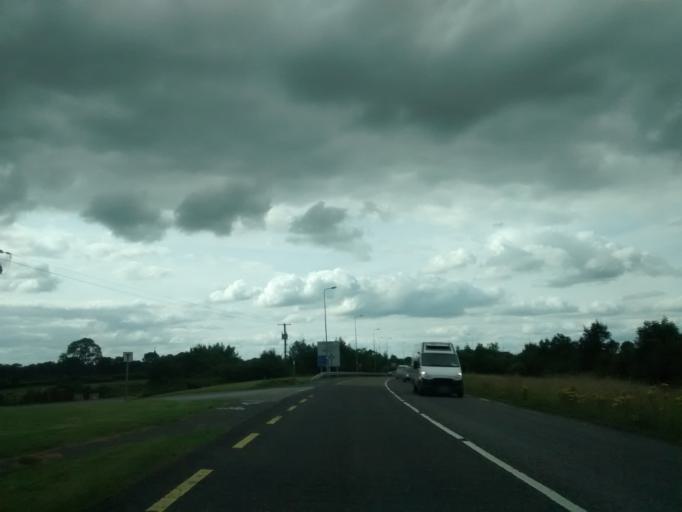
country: IE
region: Leinster
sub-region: An Iarmhi
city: Moate
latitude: 53.3844
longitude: -7.6807
